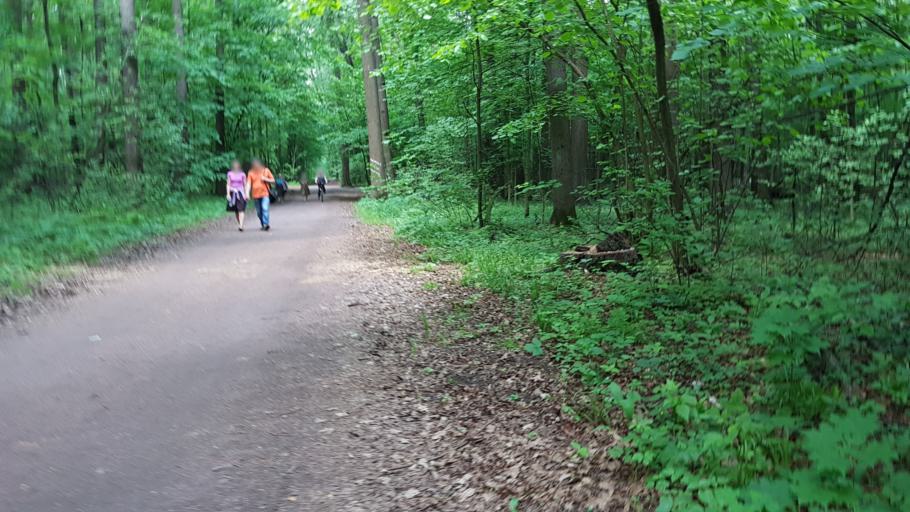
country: RU
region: Moskovskaya
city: Izmaylovo
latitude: 55.7727
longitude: 37.7712
